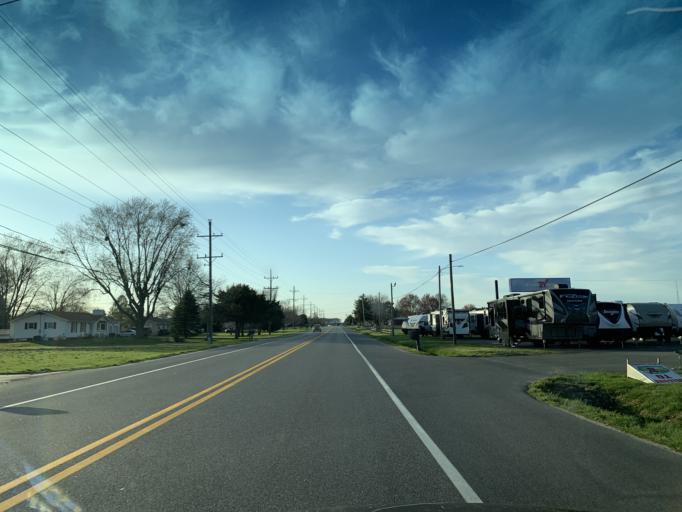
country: US
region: Delaware
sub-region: Sussex County
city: Milford
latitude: 38.9232
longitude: -75.4536
